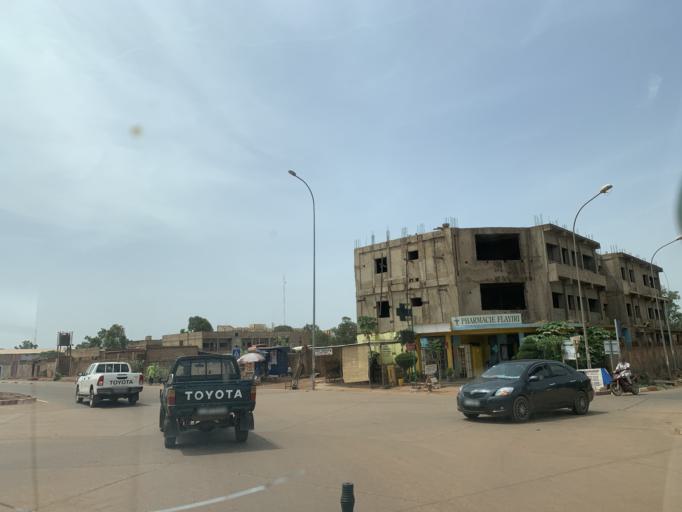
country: BF
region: Centre
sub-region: Kadiogo Province
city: Ouagadougou
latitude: 12.3371
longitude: -1.5082
